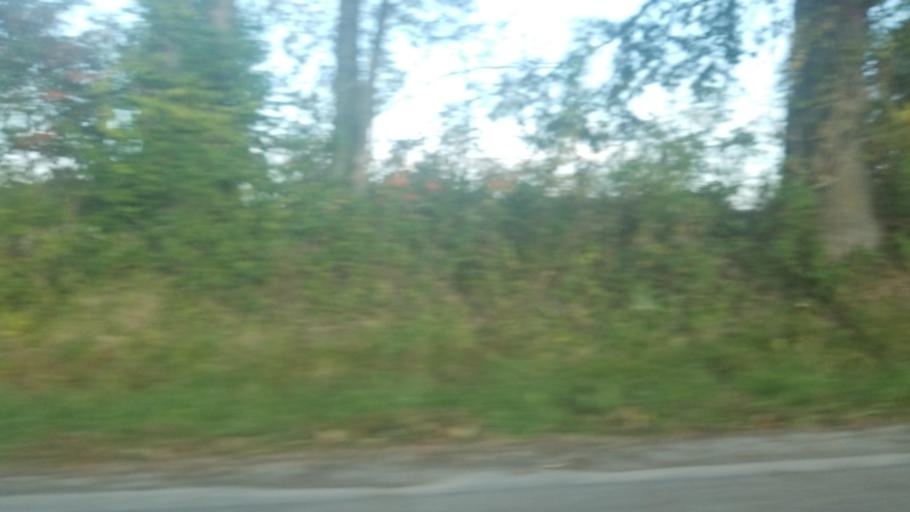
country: US
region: Illinois
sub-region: Saline County
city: Harrisburg
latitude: 37.8330
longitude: -88.6146
